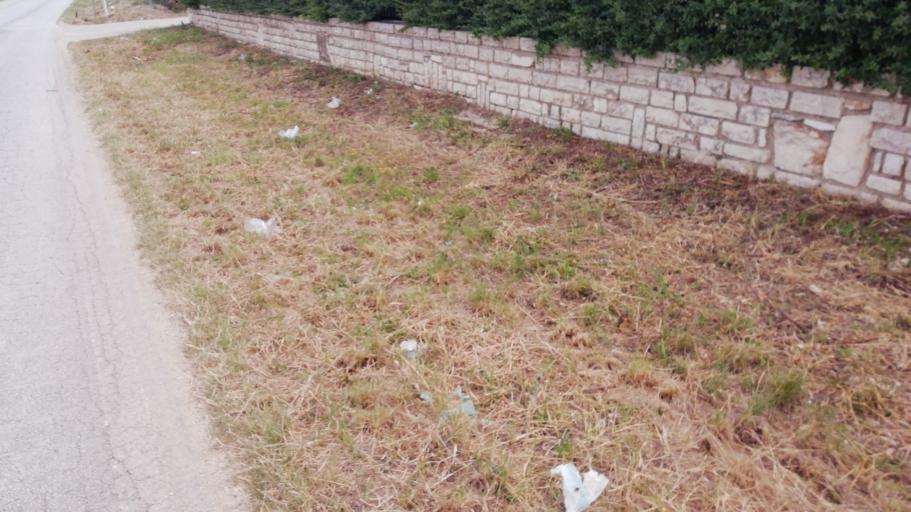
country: IT
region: Apulia
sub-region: Provincia di Bari
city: Corato
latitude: 41.1124
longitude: 16.3658
